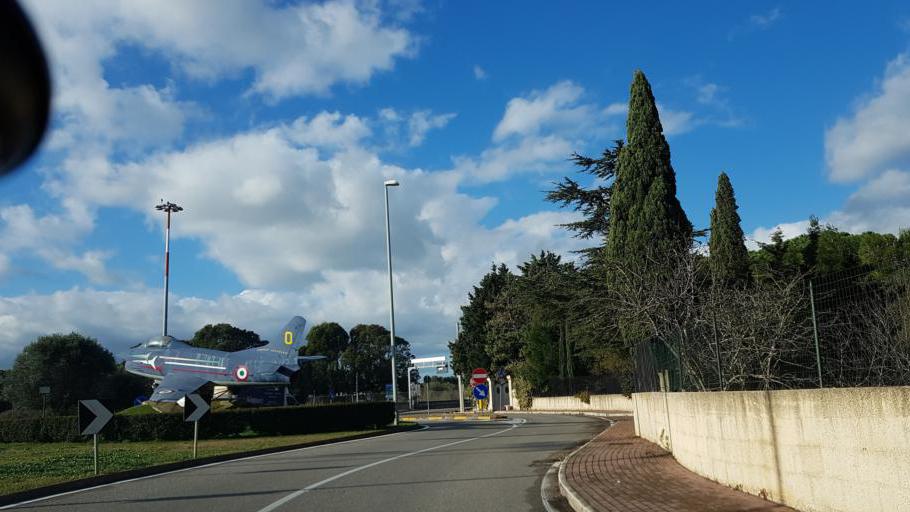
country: IT
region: Apulia
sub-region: Provincia di Brindisi
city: Materdomini
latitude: 40.6581
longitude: 17.9371
